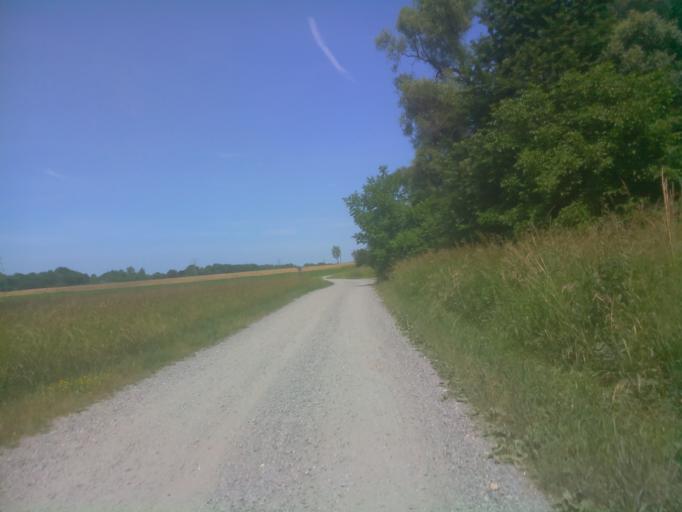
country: DE
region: Hesse
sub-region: Regierungsbezirk Darmstadt
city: Bensheim
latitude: 49.6597
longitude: 8.6118
